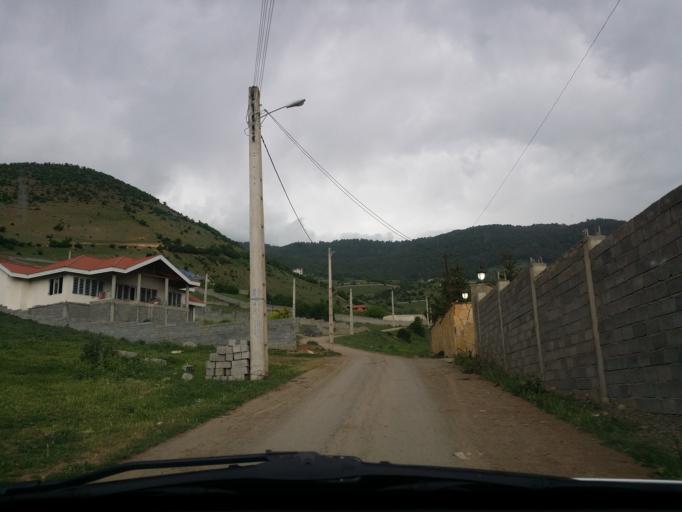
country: IR
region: Mazandaran
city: `Abbasabad
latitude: 36.5066
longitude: 51.1415
